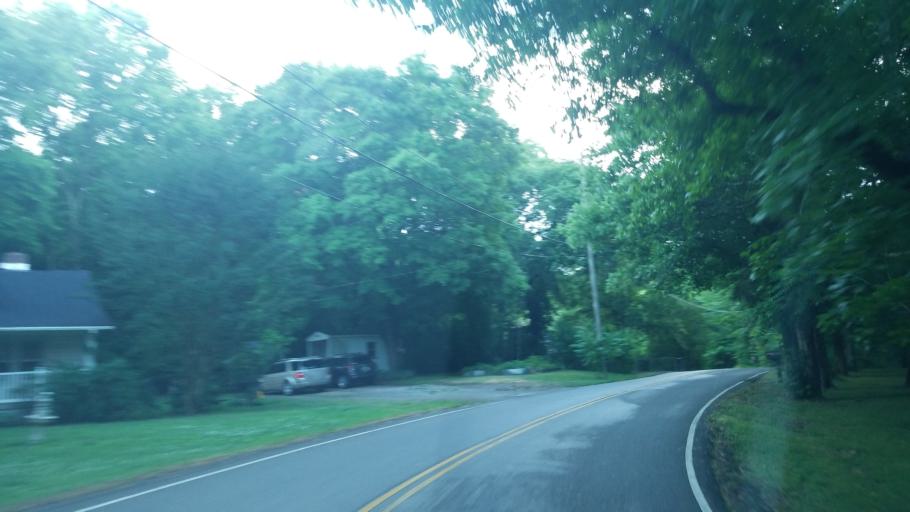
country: US
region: Tennessee
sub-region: Rutherford County
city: La Vergne
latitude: 36.1168
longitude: -86.6355
